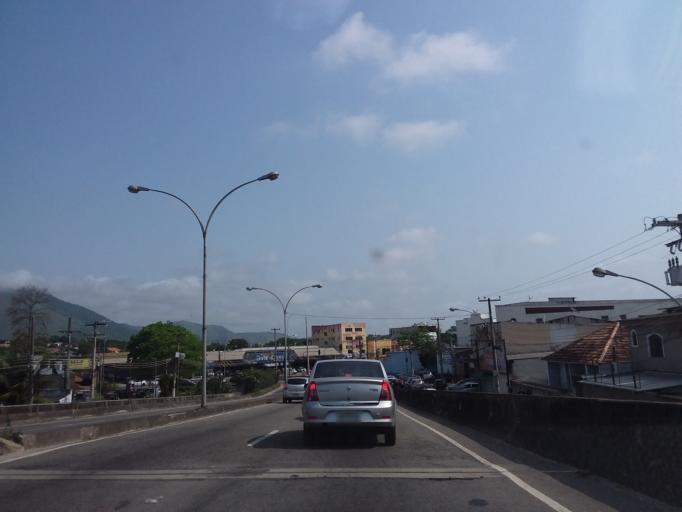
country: BR
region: Rio de Janeiro
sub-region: Nilopolis
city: Nilopolis
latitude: -22.9013
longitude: -43.5501
